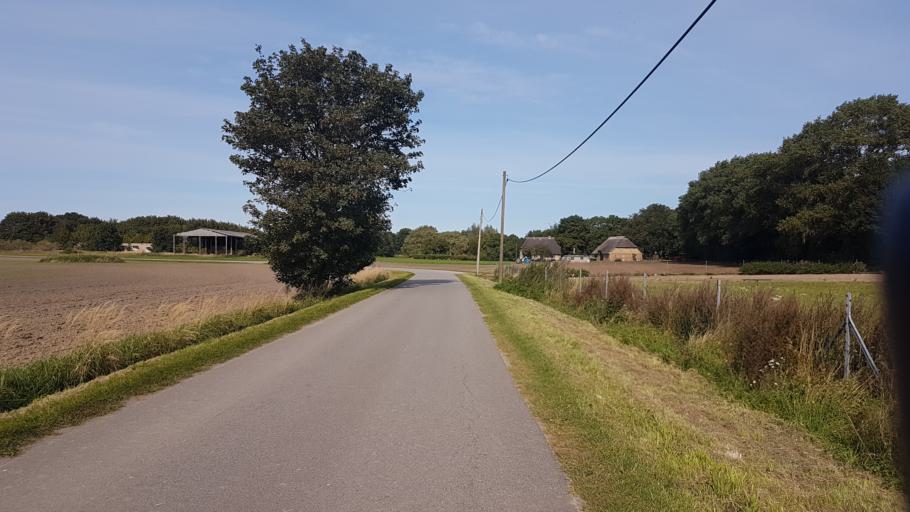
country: DE
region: Mecklenburg-Vorpommern
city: Gingst
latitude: 54.4335
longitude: 13.2240
